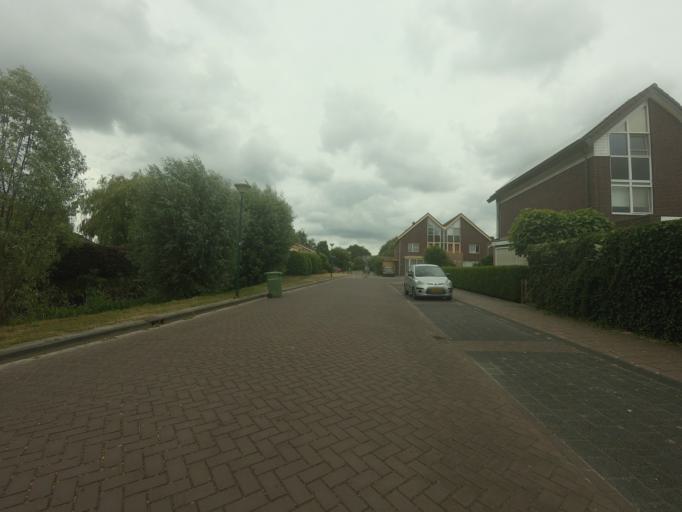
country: NL
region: Utrecht
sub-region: Gemeente Soest
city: Soest
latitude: 52.1724
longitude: 5.2678
